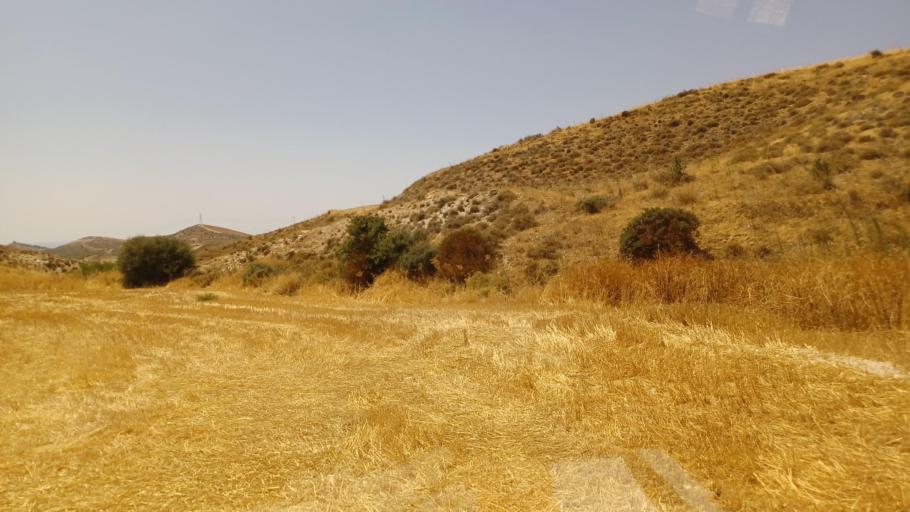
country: CY
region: Larnaka
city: Athienou
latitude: 35.0073
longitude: 33.5535
